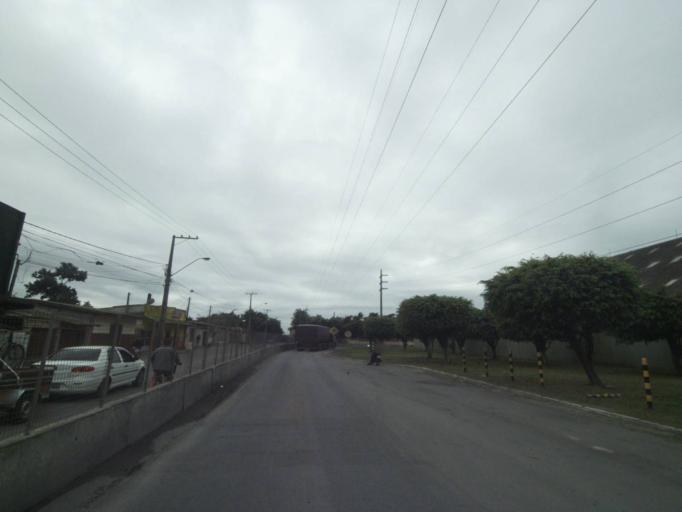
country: BR
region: Parana
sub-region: Paranagua
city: Paranagua
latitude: -25.5362
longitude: -48.5379
